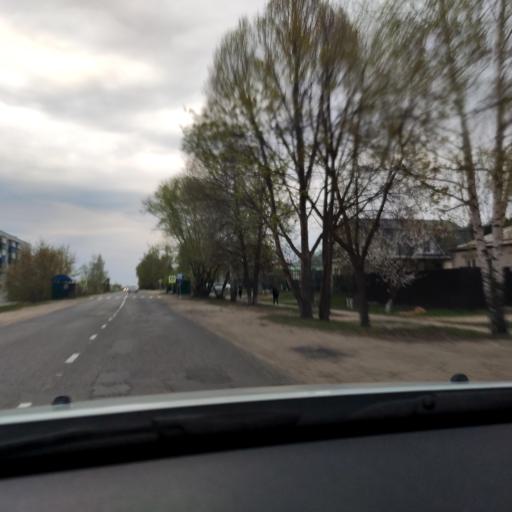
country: RU
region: Lipetsk
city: Zadonsk
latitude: 52.4050
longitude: 38.9211
